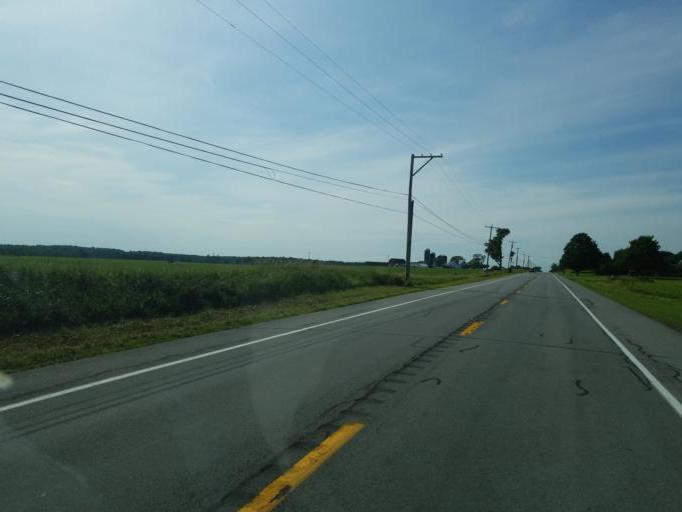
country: US
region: New York
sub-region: Livingston County
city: Caledonia
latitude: 42.9471
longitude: -77.8231
